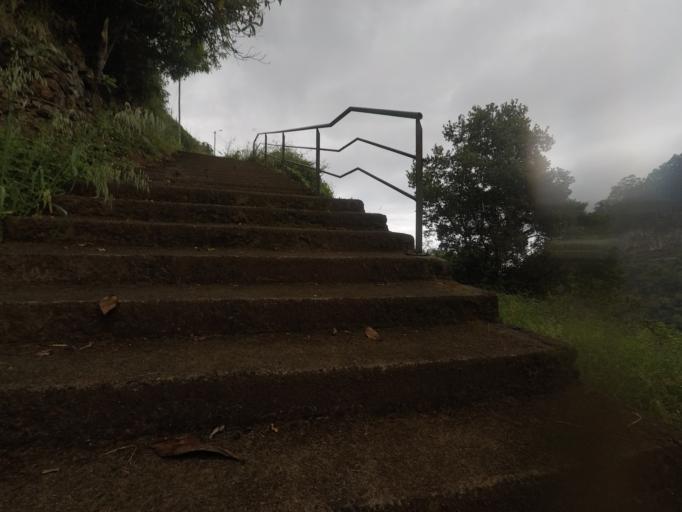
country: PT
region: Madeira
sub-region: Santana
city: Santana
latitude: 32.7681
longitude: -16.8759
